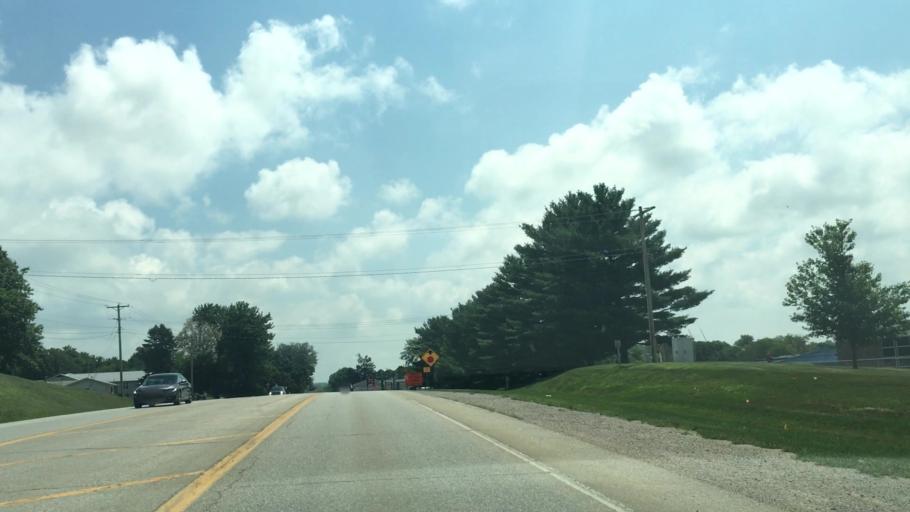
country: US
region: Iowa
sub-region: Johnson County
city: Tiffin
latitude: 41.7075
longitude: -91.6698
